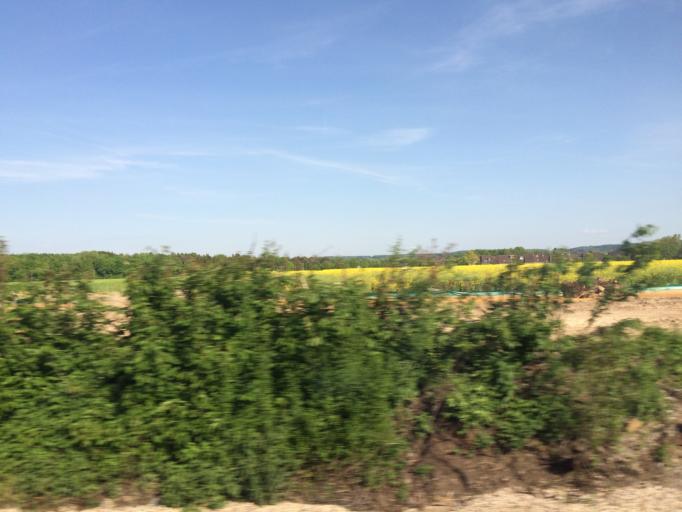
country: DE
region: North Rhine-Westphalia
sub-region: Regierungsbezirk Koln
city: Troisdorf
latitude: 50.7635
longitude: 7.1396
